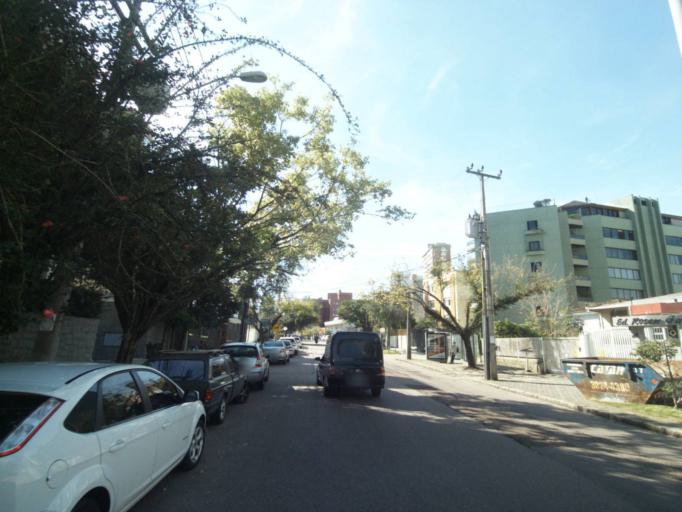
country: BR
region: Parana
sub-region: Curitiba
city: Curitiba
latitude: -25.4470
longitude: -49.2953
